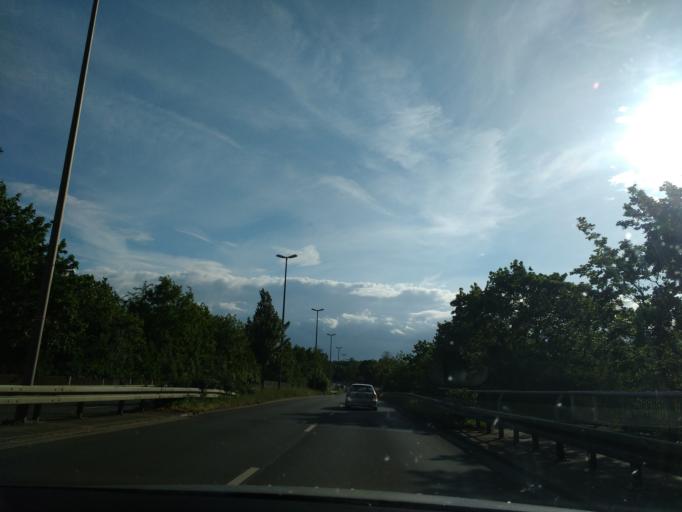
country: DE
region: North Rhine-Westphalia
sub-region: Regierungsbezirk Detmold
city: Bad Salzuflen
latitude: 52.0734
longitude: 8.7511
